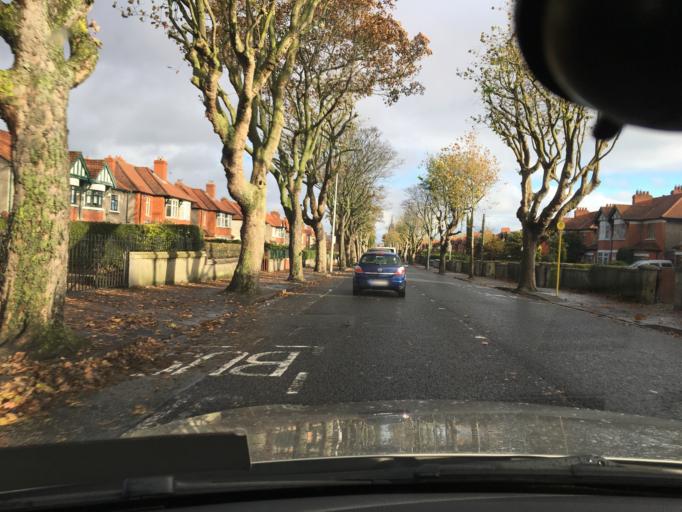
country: IE
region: Leinster
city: Cabra
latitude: 53.3613
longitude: -6.2897
